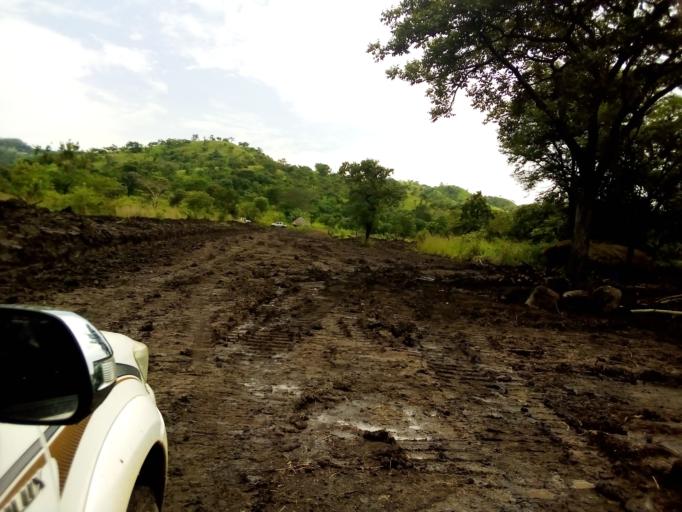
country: ET
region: Oromiya
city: Jima
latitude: 7.2162
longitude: 37.1326
